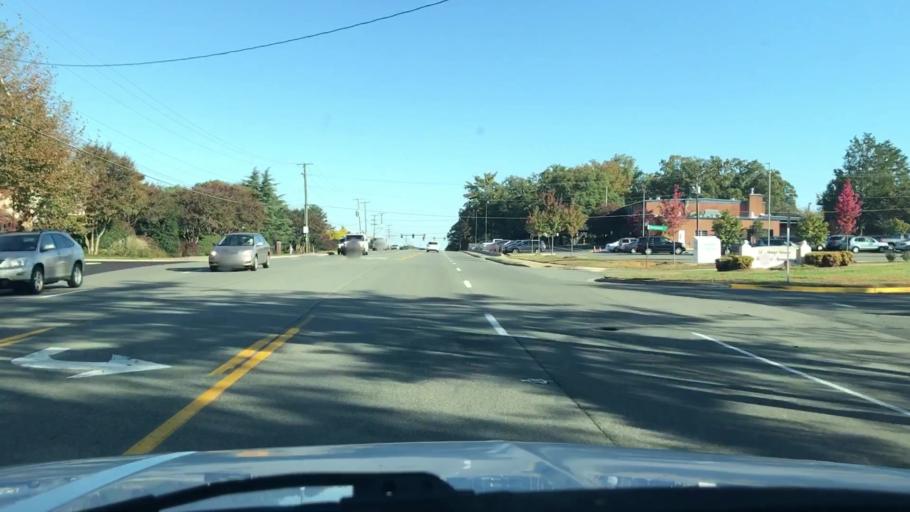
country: US
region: Virginia
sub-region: Henrico County
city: Tuckahoe
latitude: 37.6010
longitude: -77.5915
